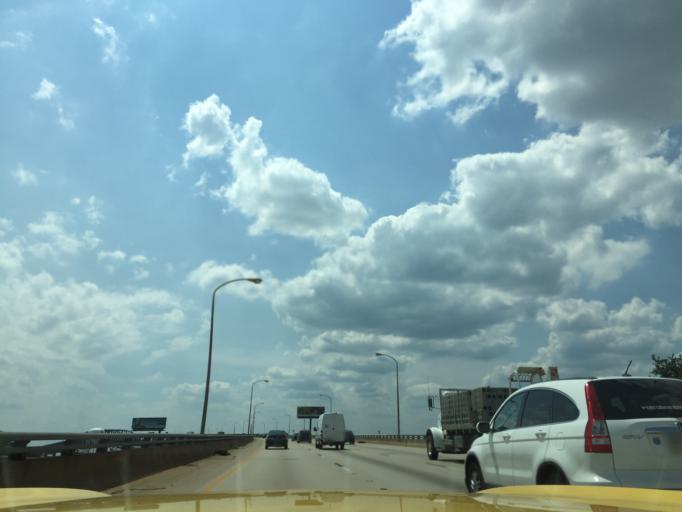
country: US
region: New Jersey
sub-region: Gloucester County
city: National Park
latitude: 39.8979
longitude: -75.1853
